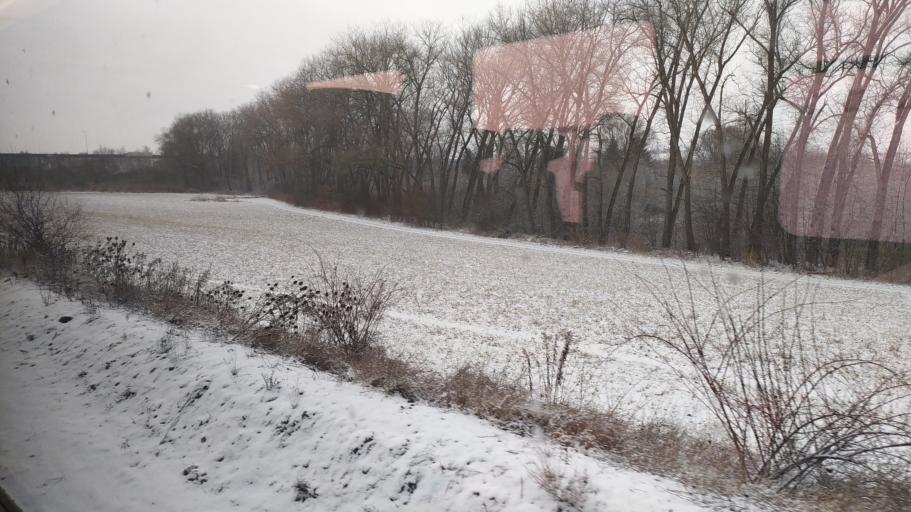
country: CZ
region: Central Bohemia
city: Trebotov
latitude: 50.0289
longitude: 14.2939
